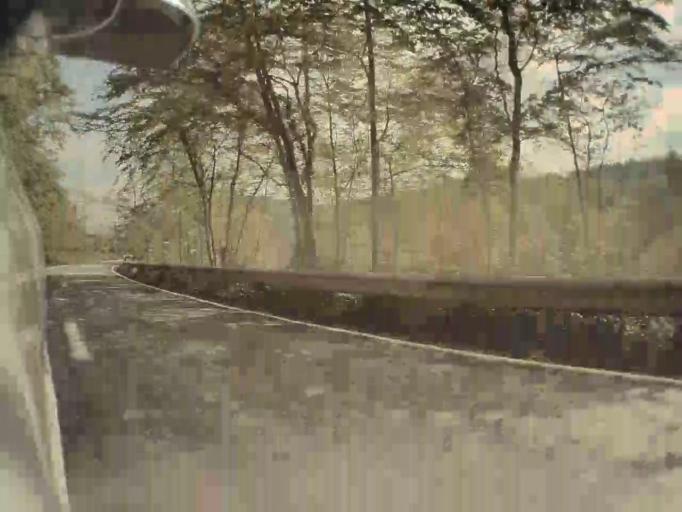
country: BE
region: Wallonia
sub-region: Province du Luxembourg
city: Tellin
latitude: 50.0766
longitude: 5.2082
